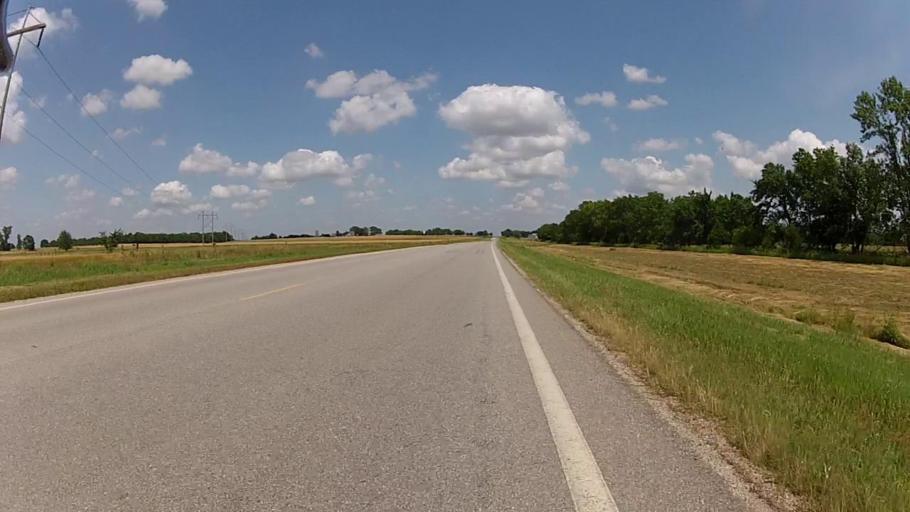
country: US
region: Kansas
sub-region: Labette County
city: Altamont
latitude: 37.1938
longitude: -95.2584
